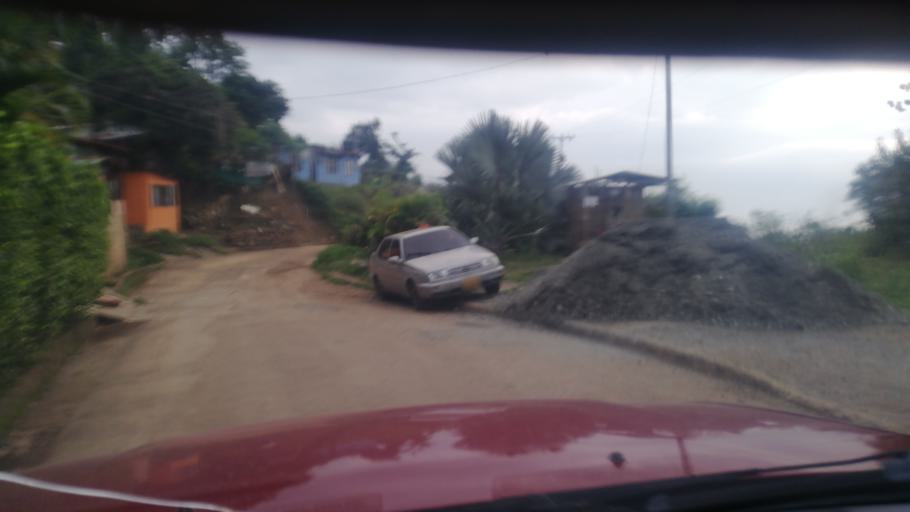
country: CO
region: Valle del Cauca
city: Cali
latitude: 3.5029
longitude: -76.5464
